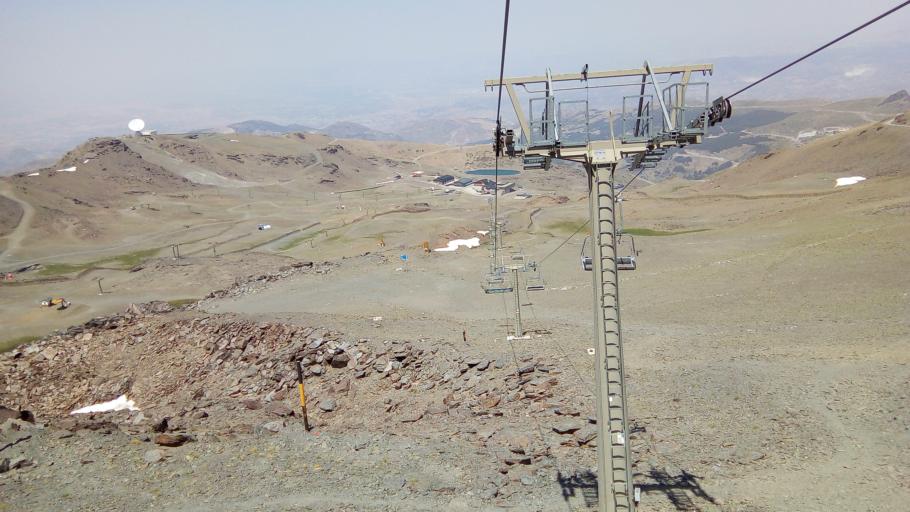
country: ES
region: Andalusia
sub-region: Provincia de Granada
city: Capileira
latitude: 37.0628
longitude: -3.3741
